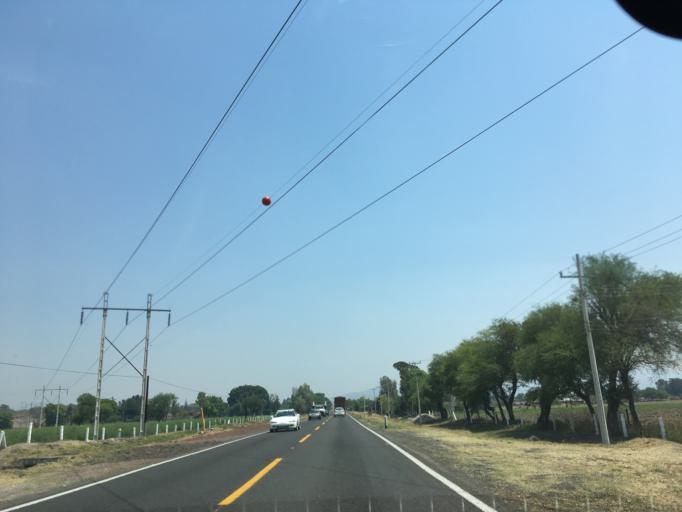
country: MX
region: Michoacan
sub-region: Cuitzeo
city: Cuamio
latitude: 20.0187
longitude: -101.1541
